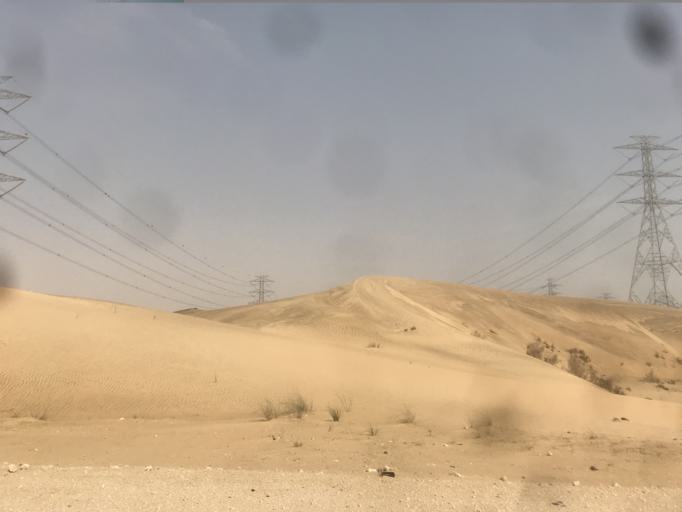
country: SA
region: Eastern Province
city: Abqaiq
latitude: 25.9073
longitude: 49.9050
